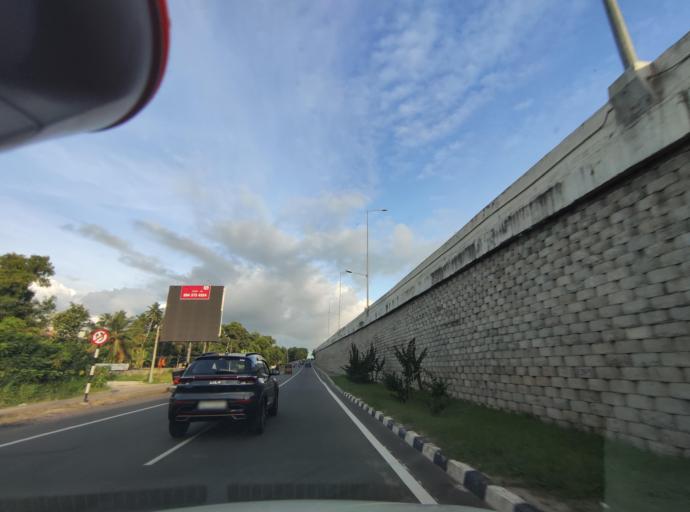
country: IN
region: Kerala
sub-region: Thiruvananthapuram
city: Thiruvananthapuram
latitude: 8.4987
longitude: 76.9166
